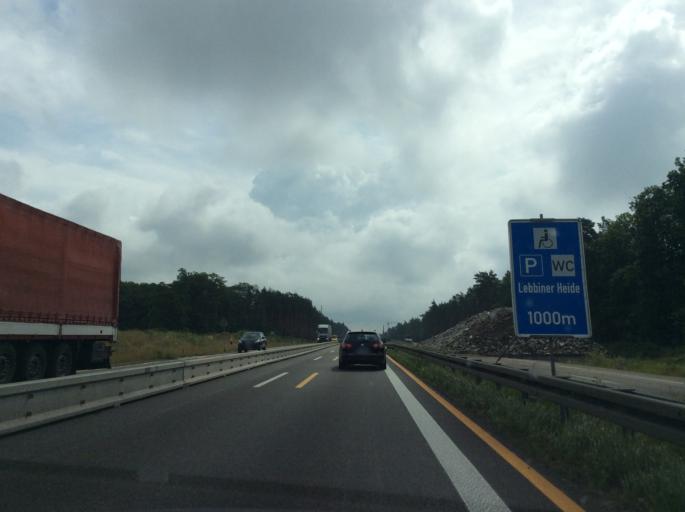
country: DE
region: Brandenburg
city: Storkow
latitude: 52.3126
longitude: 13.9330
